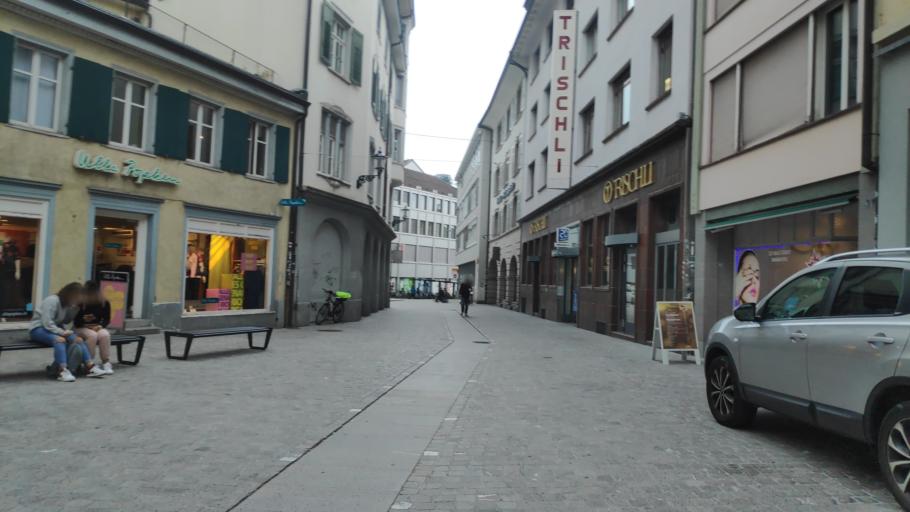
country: CH
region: Saint Gallen
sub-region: Wahlkreis St. Gallen
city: Sankt Gallen
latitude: 47.4256
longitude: 9.3781
